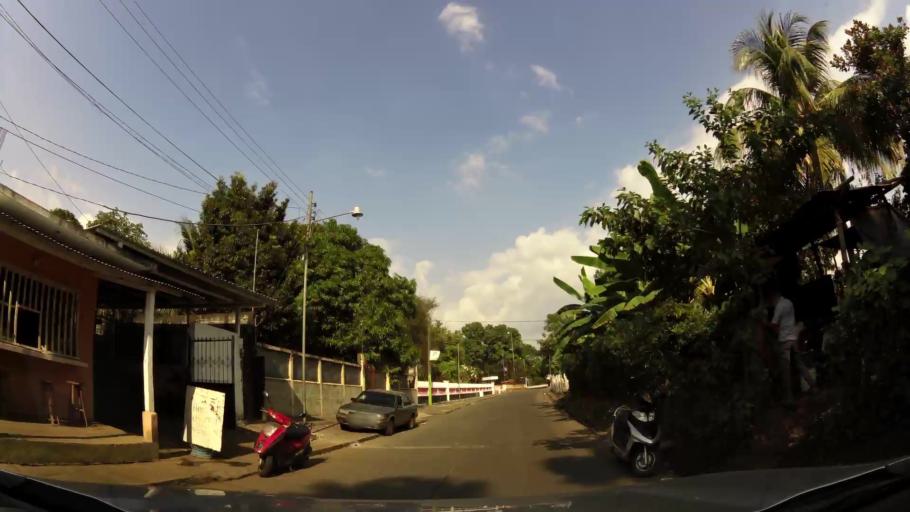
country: GT
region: Retalhuleu
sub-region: Municipio de Retalhuleu
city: Retalhuleu
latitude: 14.5371
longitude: -91.6873
